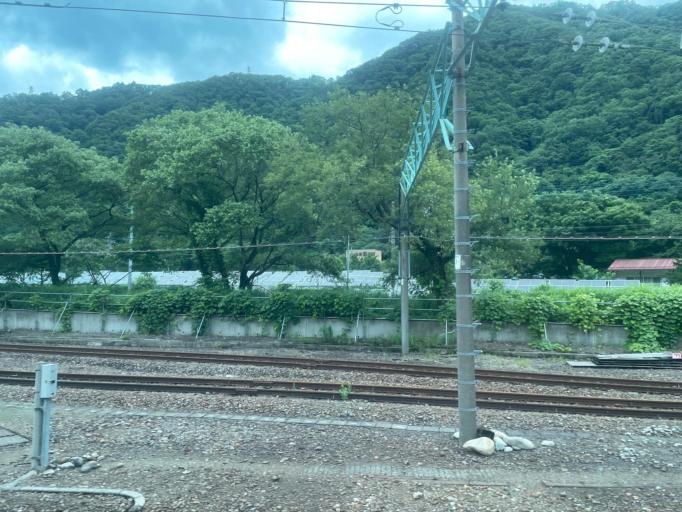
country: JP
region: Gunma
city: Numata
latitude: 36.7817
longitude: 138.9706
